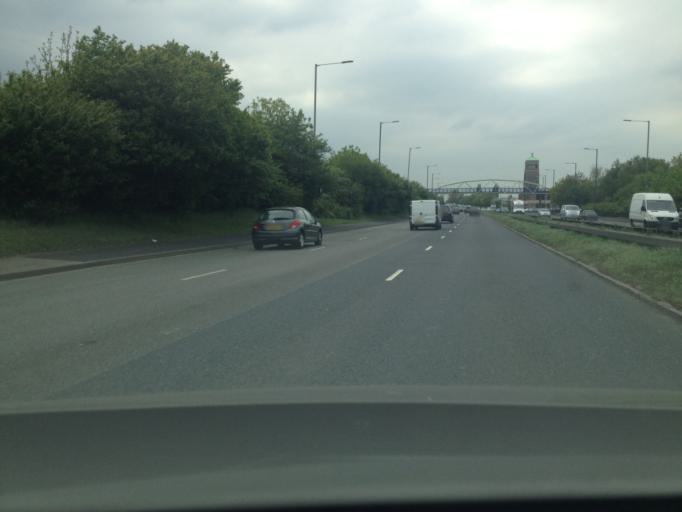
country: GB
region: England
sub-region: Greater London
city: Greenford
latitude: 51.5381
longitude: -0.3563
